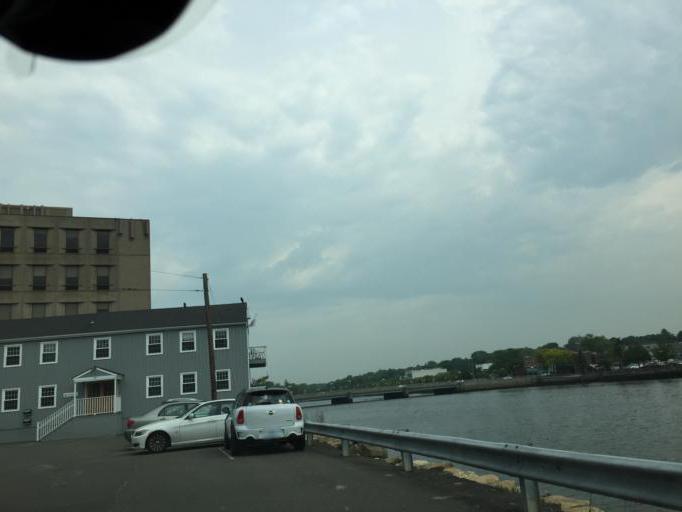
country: US
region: Connecticut
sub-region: Fairfield County
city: Westport
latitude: 41.1388
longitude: -73.3634
